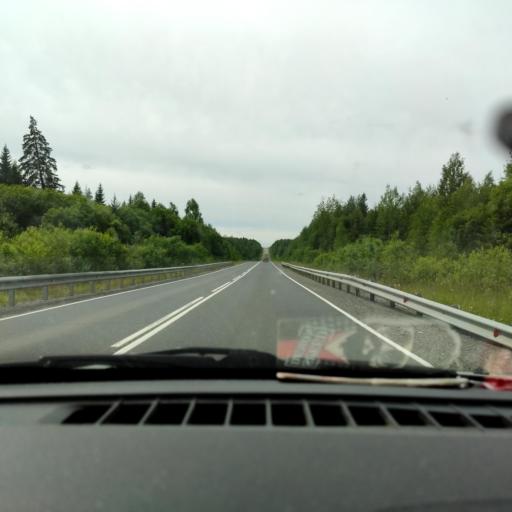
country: RU
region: Perm
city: Chusovoy
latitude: 58.3732
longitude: 57.9881
